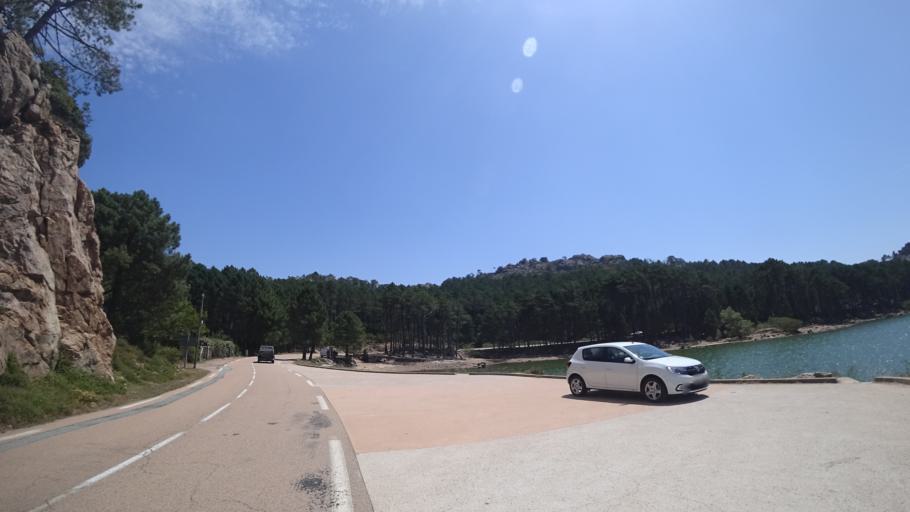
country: FR
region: Corsica
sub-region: Departement de la Corse-du-Sud
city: Zonza
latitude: 41.6682
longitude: 9.2082
